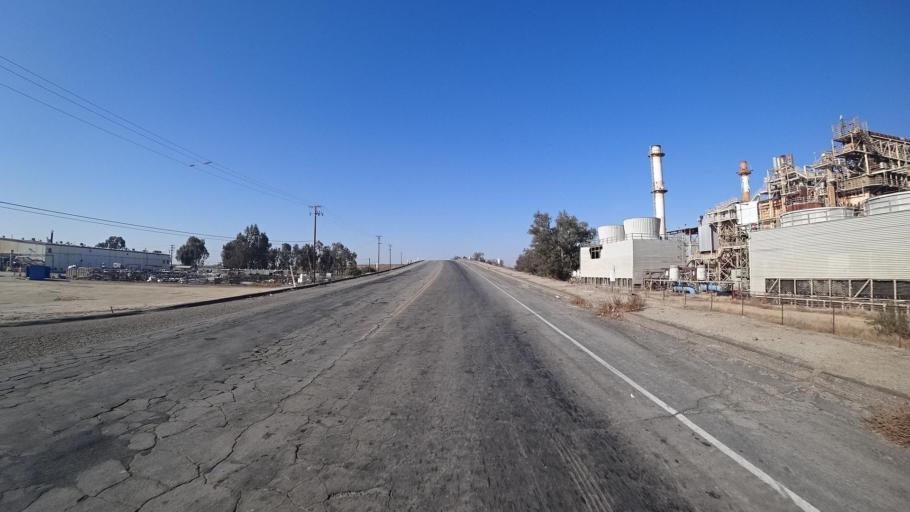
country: US
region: California
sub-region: Kern County
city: McFarland
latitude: 35.7180
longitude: -119.2337
